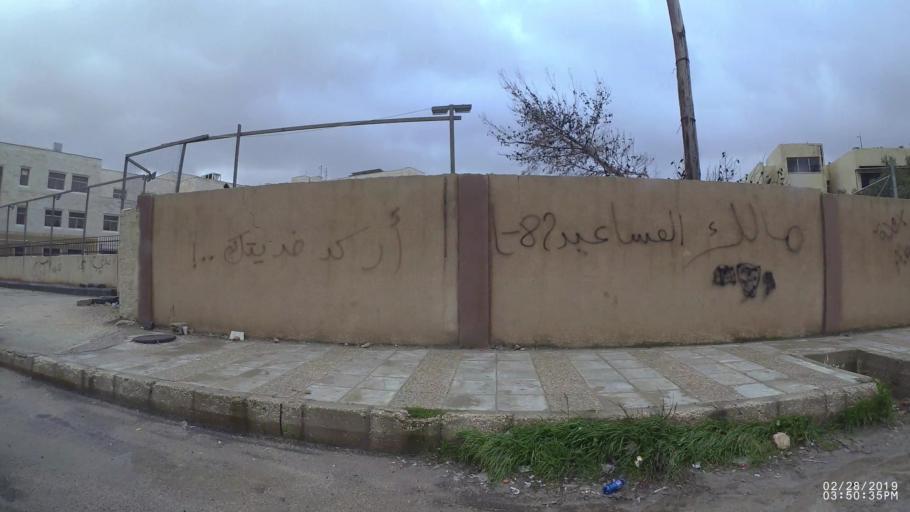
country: JO
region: Amman
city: Amman
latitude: 31.9954
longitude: 35.9256
